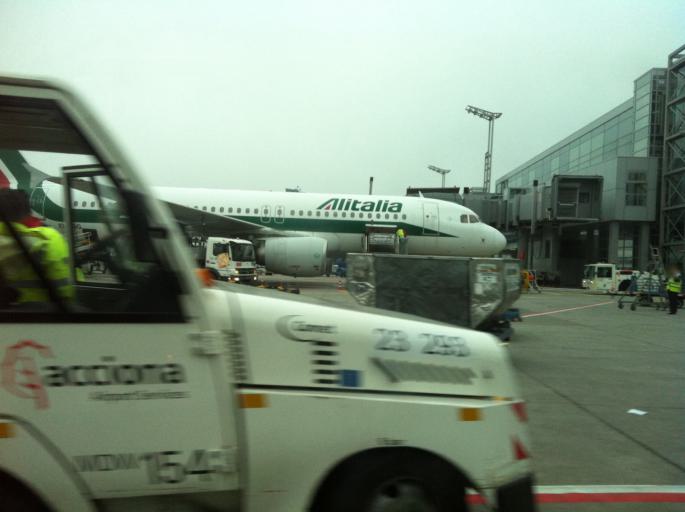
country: DE
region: Hesse
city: Niederrad
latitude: 50.0509
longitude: 8.5883
